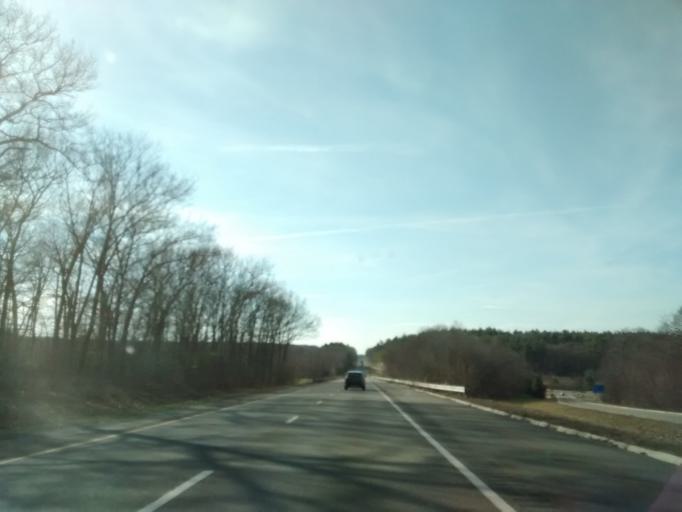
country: US
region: Massachusetts
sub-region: Worcester County
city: Uxbridge
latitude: 42.0655
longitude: -71.6624
